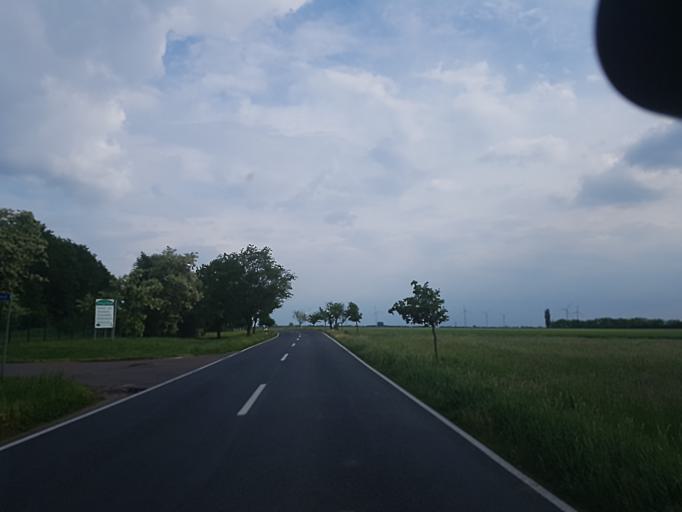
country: DE
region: Saxony-Anhalt
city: Klieken
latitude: 51.9229
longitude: 12.3920
